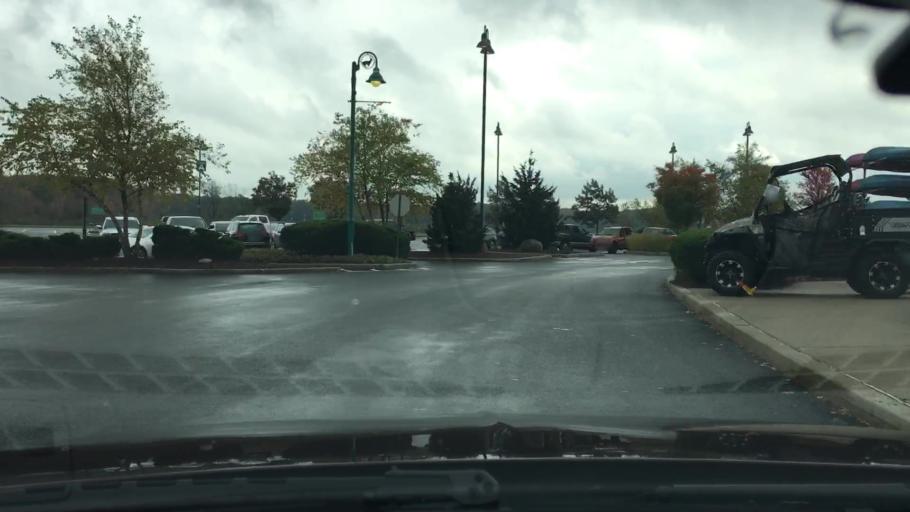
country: US
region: Connecticut
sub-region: Hartford County
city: East Hartford
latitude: 41.7562
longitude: -72.6216
